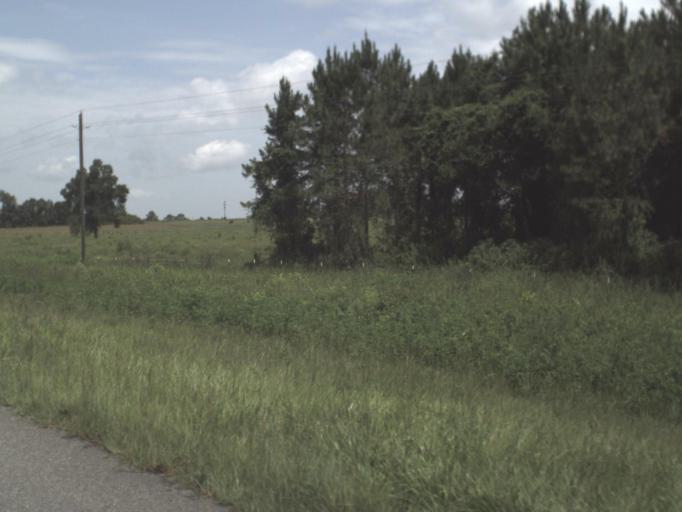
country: US
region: Florida
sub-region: Madison County
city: Madison
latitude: 30.4705
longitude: -83.5947
